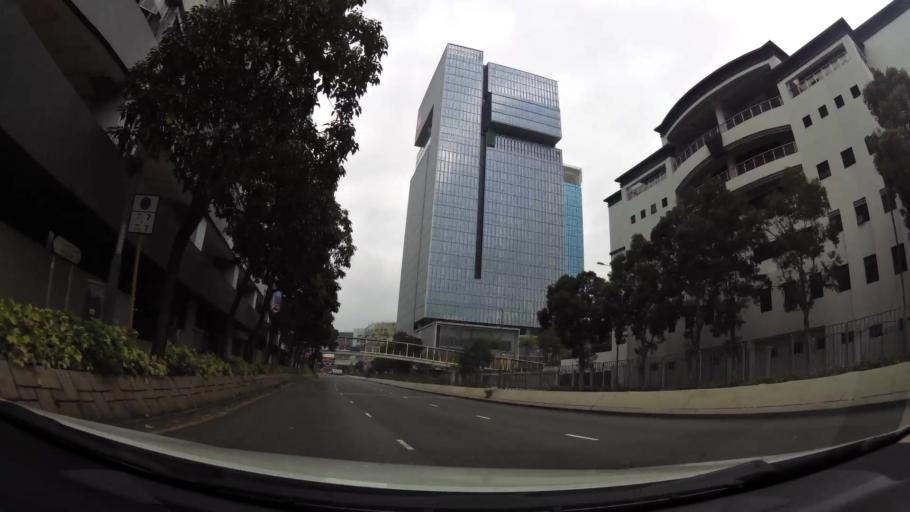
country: HK
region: Kowloon City
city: Kowloon
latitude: 22.3255
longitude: 114.2084
